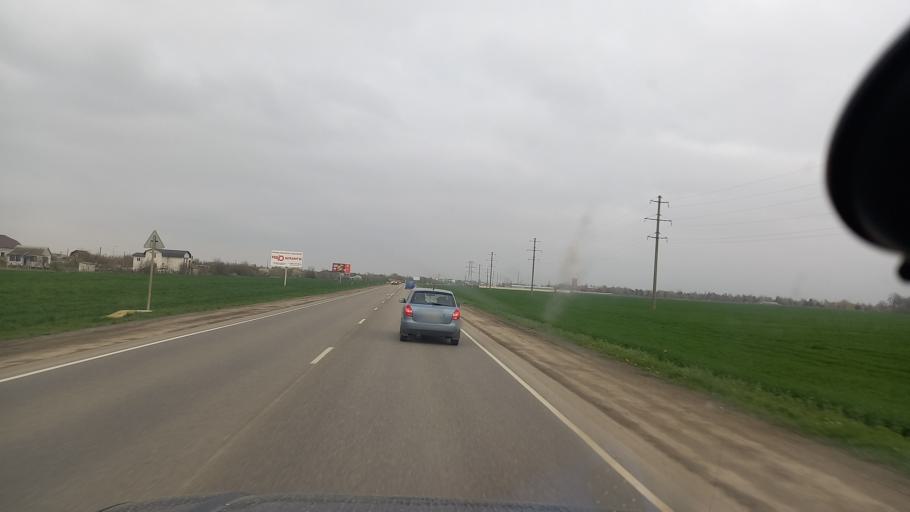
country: RU
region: Krasnodarskiy
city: Slavyansk-na-Kubani
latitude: 45.2467
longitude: 38.0574
